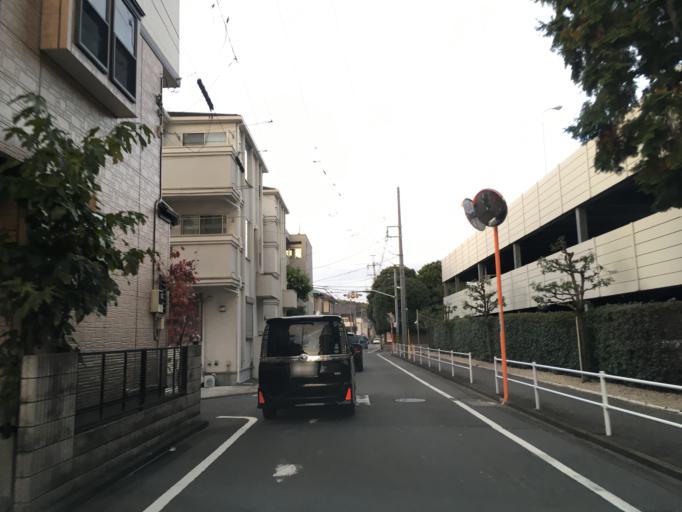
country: JP
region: Tokyo
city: Hachioji
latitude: 35.5969
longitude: 139.3512
